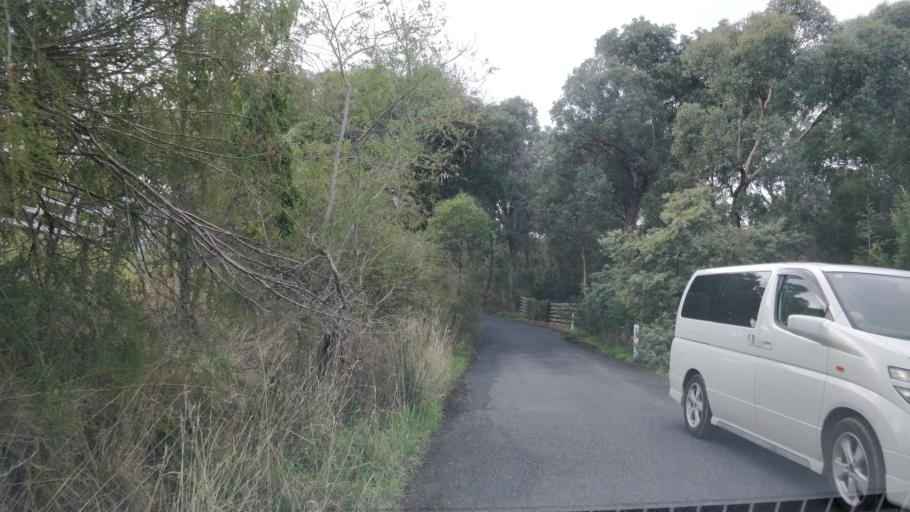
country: AU
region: Victoria
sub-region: Nillumbik
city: Research
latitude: -37.7163
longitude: 145.1715
